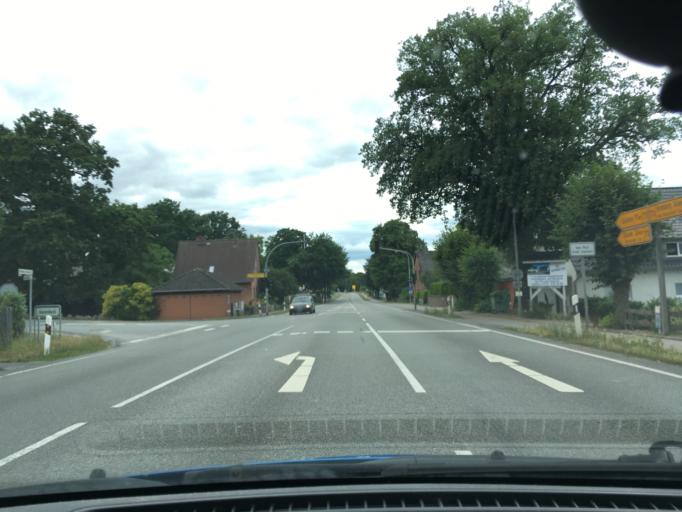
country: DE
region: Lower Saxony
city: Buxtehude
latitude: 53.4527
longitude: 9.7409
